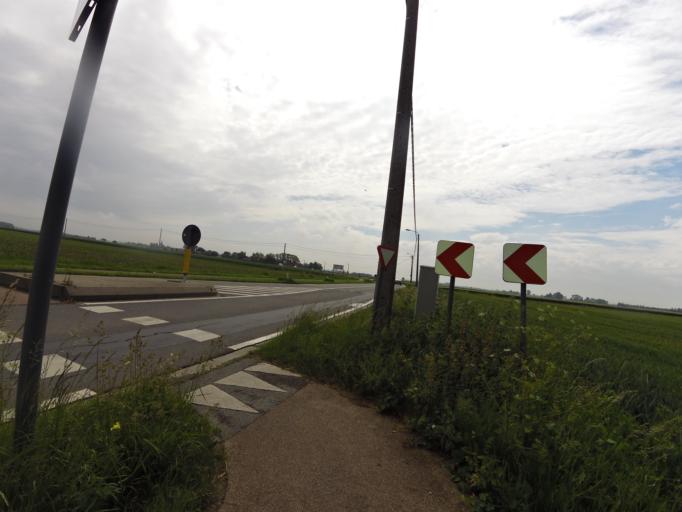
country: BE
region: Flanders
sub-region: Provincie West-Vlaanderen
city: Middelkerke
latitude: 51.1600
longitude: 2.8300
